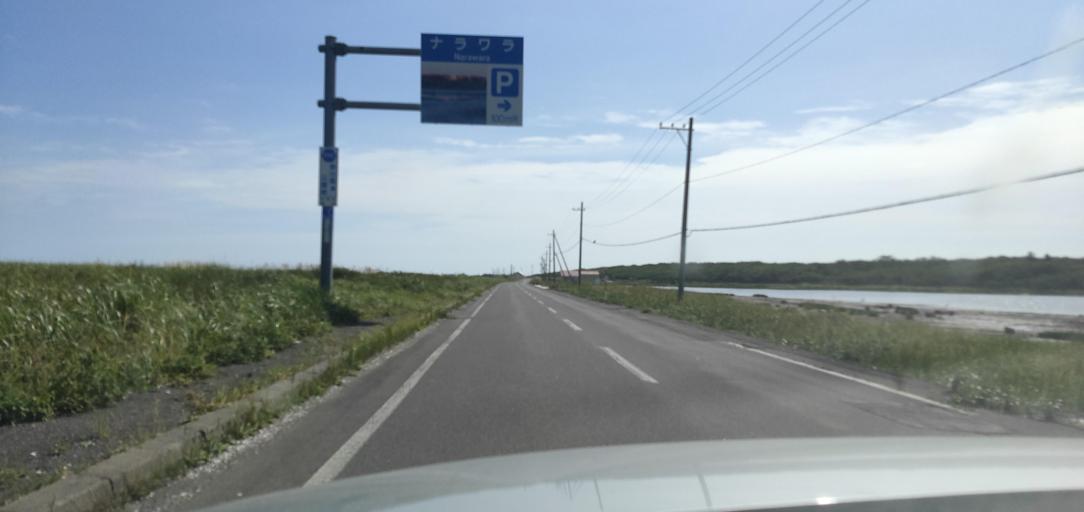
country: JP
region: Hokkaido
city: Shibetsu
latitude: 43.6094
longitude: 145.2732
